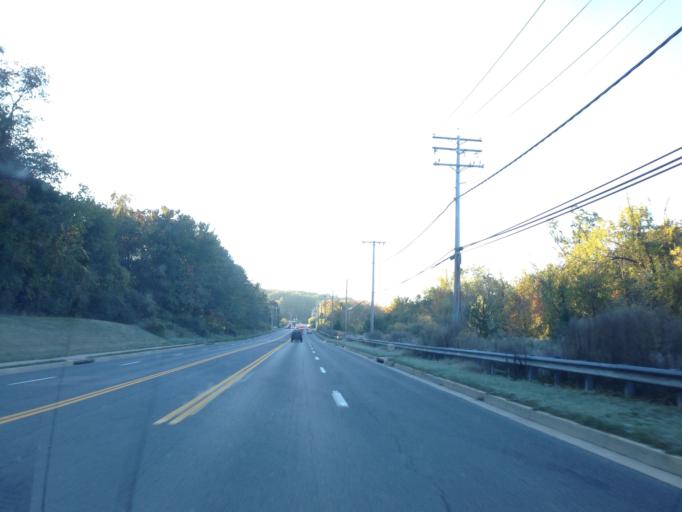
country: US
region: Maryland
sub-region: Baltimore County
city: Owings Mills
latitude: 39.4473
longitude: -76.7840
